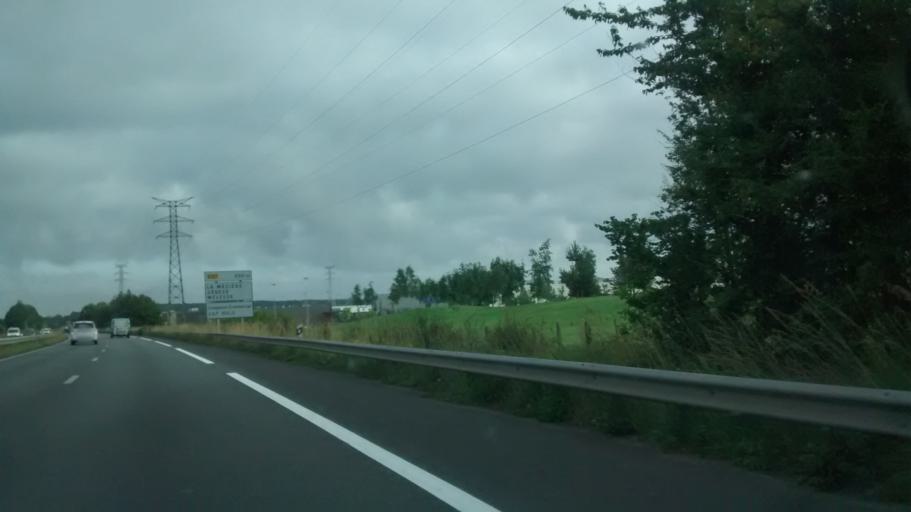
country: FR
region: Brittany
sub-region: Departement d'Ille-et-Vilaine
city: La Chapelle-des-Fougeretz
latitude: 48.1941
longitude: -1.7238
